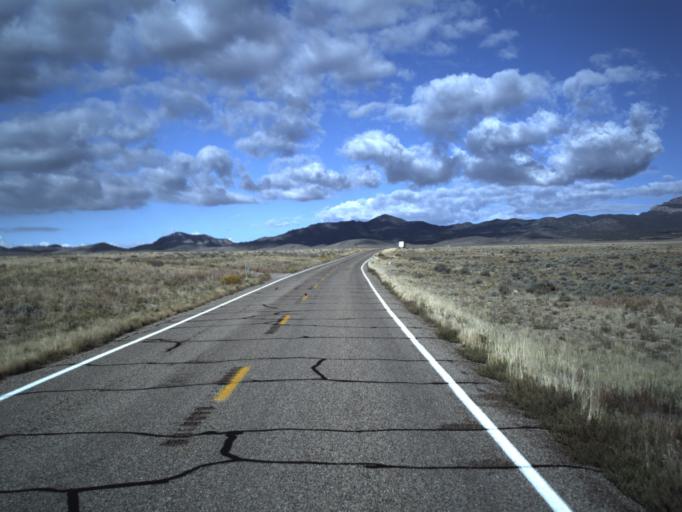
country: US
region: Utah
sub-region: Beaver County
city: Milford
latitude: 38.4417
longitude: -113.1678
